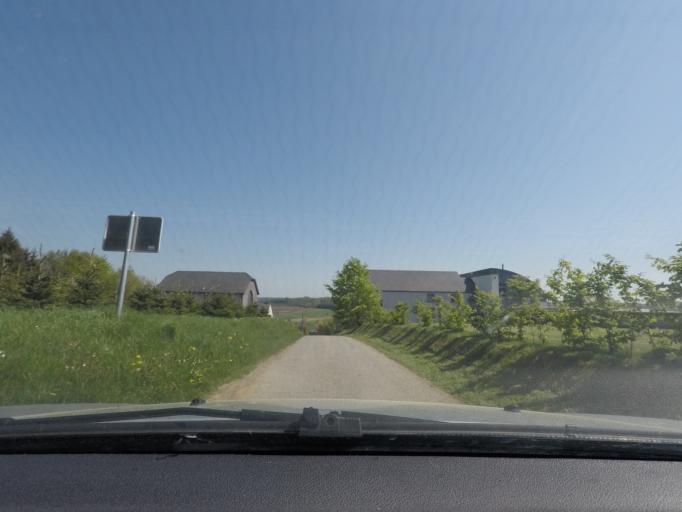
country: BE
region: Wallonia
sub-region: Province du Luxembourg
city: Leglise
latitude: 49.7867
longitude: 5.4819
